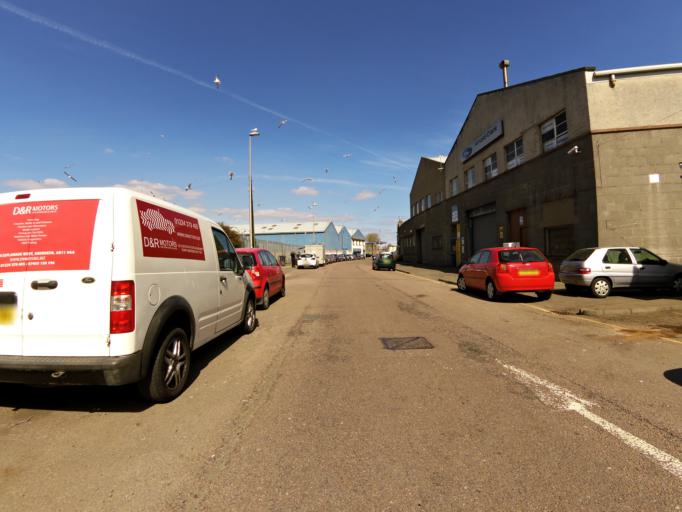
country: GB
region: Scotland
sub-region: Aberdeen City
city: Aberdeen
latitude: 57.1372
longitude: -2.0928
